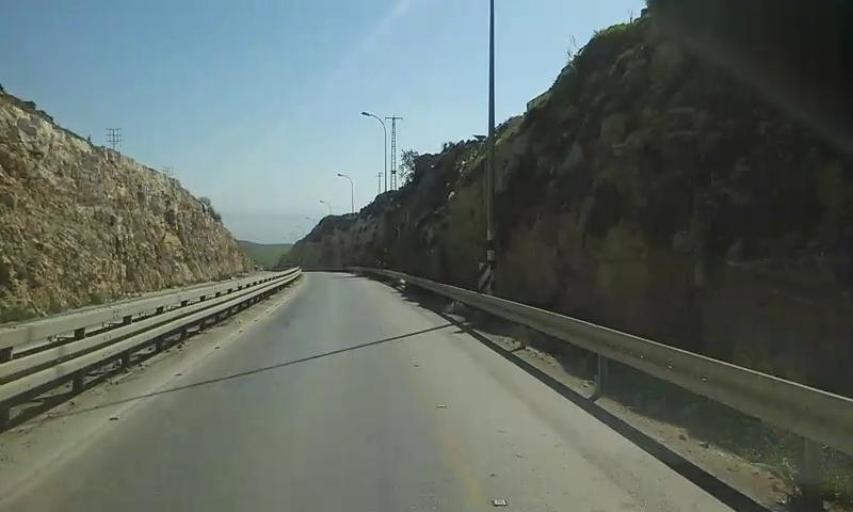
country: PS
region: West Bank
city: Jaba`
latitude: 31.8544
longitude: 35.2517
